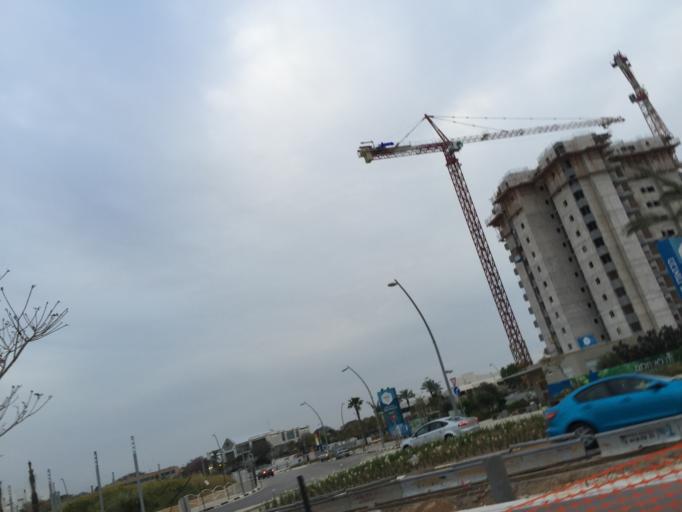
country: IL
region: Haifa
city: Qesarya
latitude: 32.5045
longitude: 34.9188
